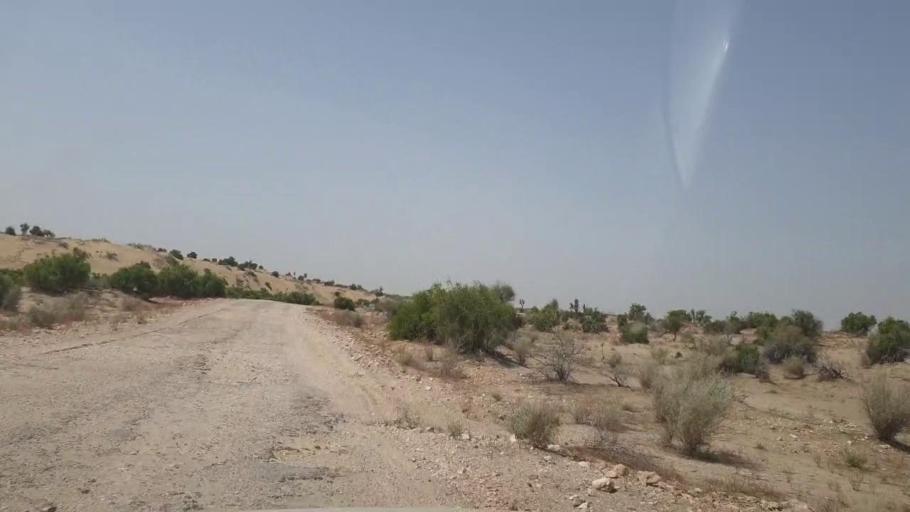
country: PK
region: Sindh
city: Khanpur
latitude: 27.3694
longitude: 69.3180
